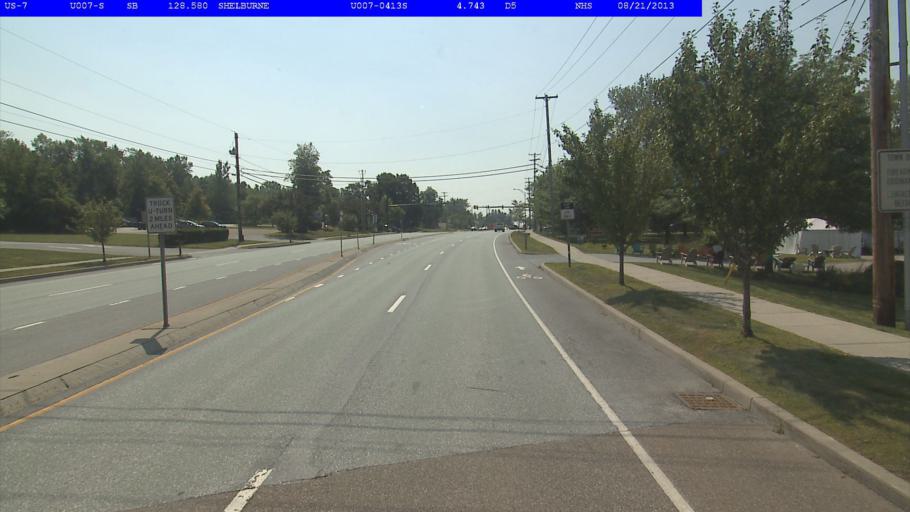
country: US
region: Vermont
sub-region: Chittenden County
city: Burlington
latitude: 44.4204
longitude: -73.2123
